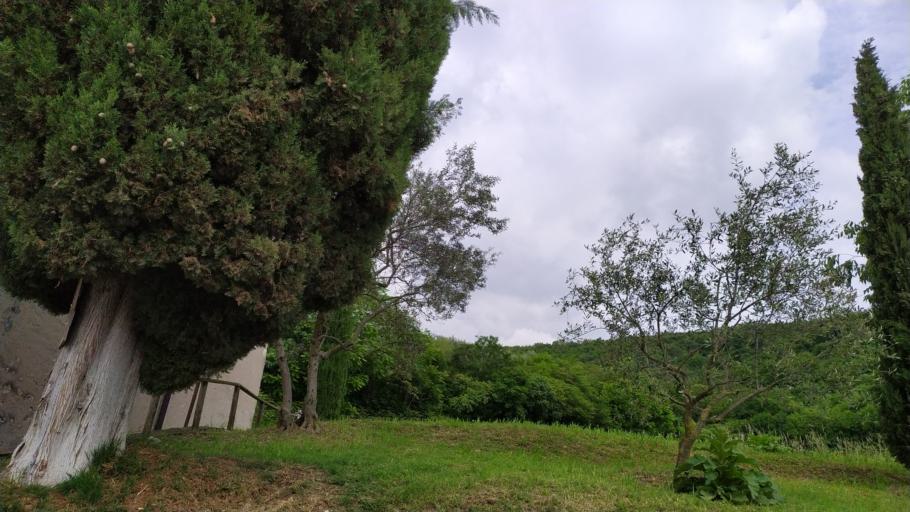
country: IT
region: Veneto
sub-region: Provincia di Verona
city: Poiano
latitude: 45.4896
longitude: 11.0374
